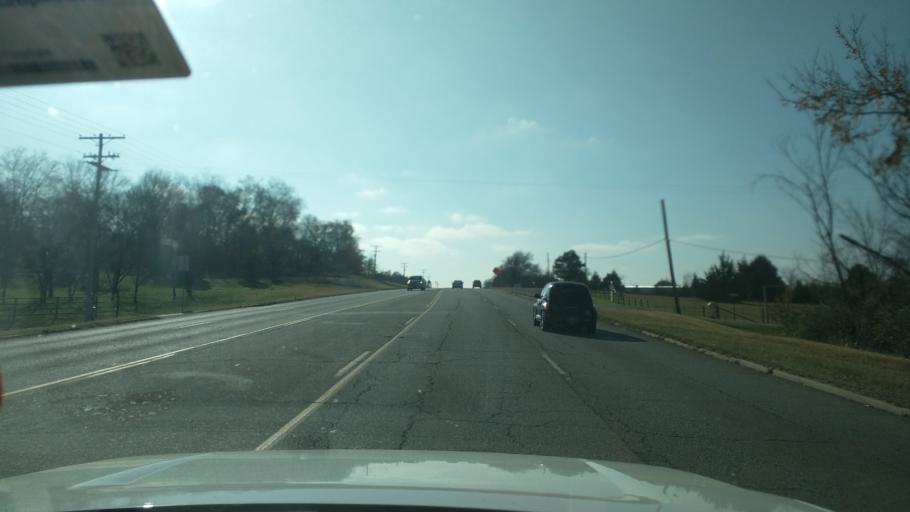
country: US
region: Oklahoma
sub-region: Washington County
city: Bartlesville
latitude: 36.6924
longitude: -95.9352
